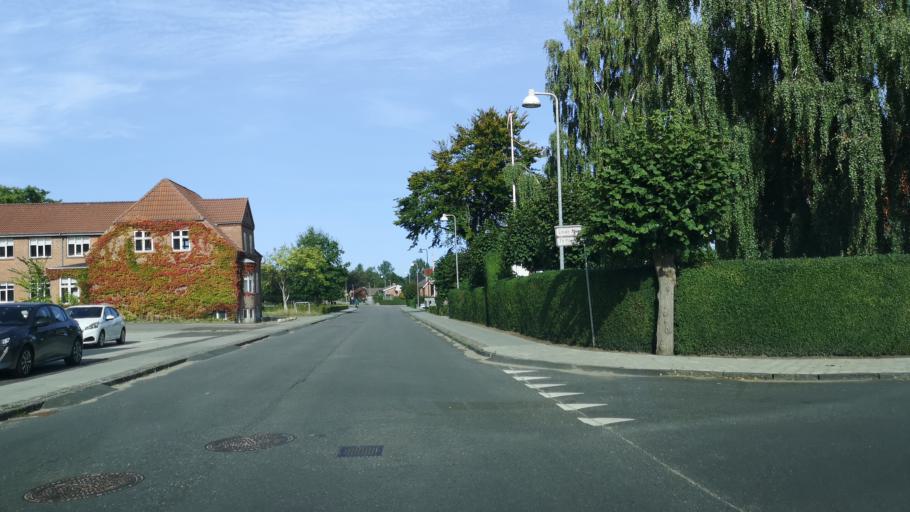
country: DK
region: Central Jutland
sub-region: Ikast-Brande Kommune
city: Ikast
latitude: 56.1458
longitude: 9.1535
